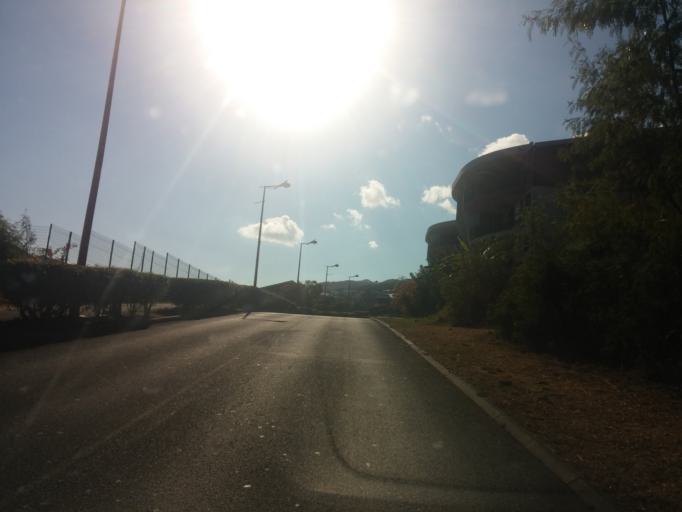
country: RE
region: Reunion
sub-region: Reunion
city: La Possession
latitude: -20.9627
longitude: 55.3293
